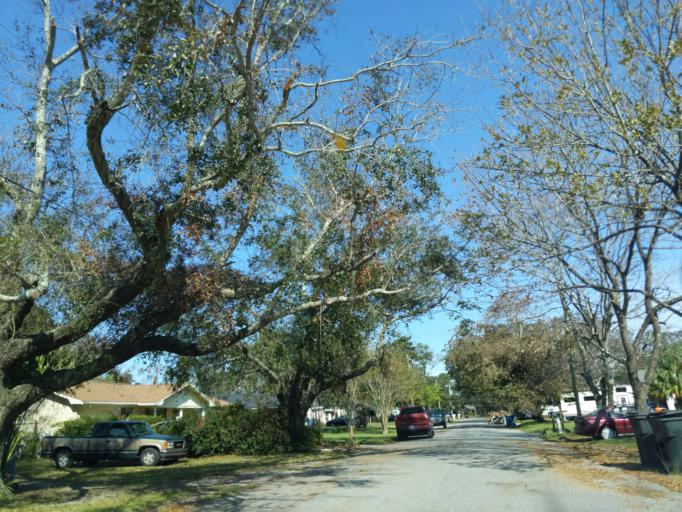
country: US
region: Florida
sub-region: Santa Rosa County
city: Gulf Breeze
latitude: 30.3556
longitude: -87.1852
